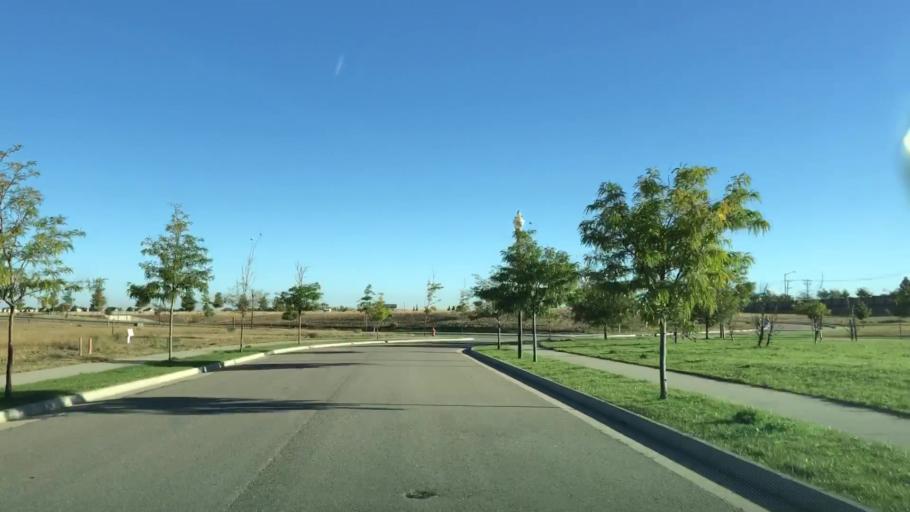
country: US
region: Colorado
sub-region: Larimer County
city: Loveland
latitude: 40.4332
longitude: -105.0218
